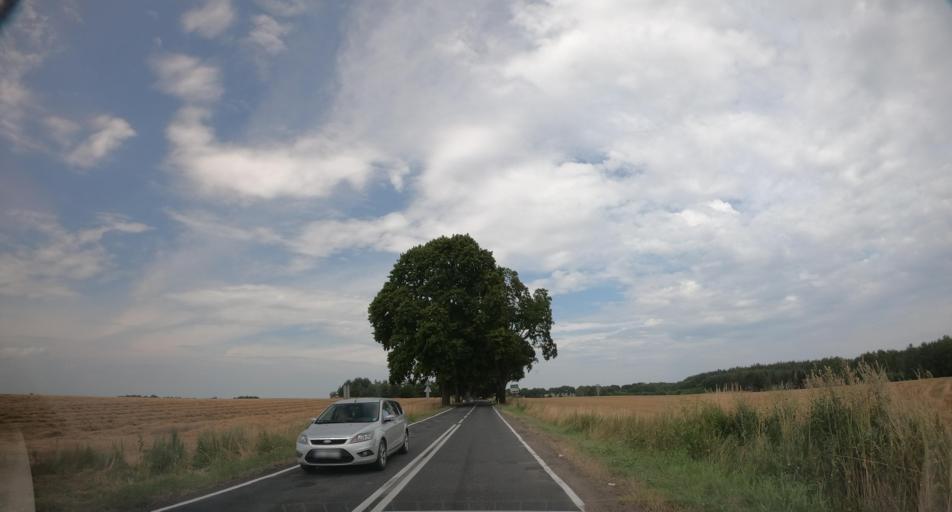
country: PL
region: West Pomeranian Voivodeship
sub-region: Powiat walecki
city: Tuczno
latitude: 53.2191
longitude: 16.1725
